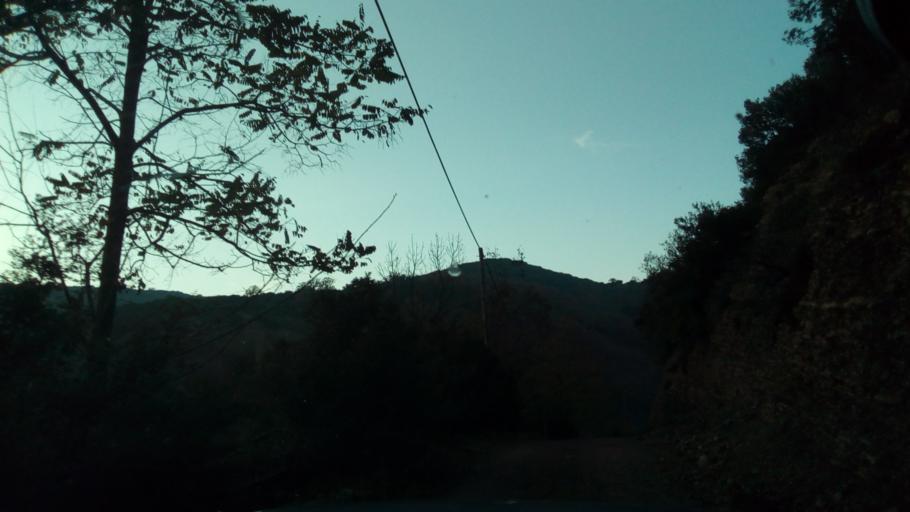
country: GR
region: West Greece
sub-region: Nomos Aitolias kai Akarnanias
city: Nafpaktos
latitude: 38.4688
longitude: 21.8151
